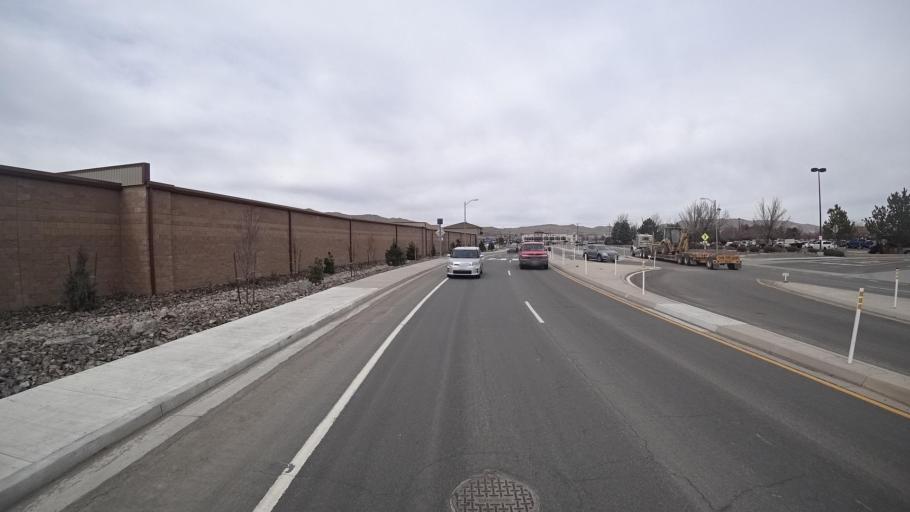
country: US
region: Nevada
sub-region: Washoe County
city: Spanish Springs
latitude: 39.6368
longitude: -119.7100
